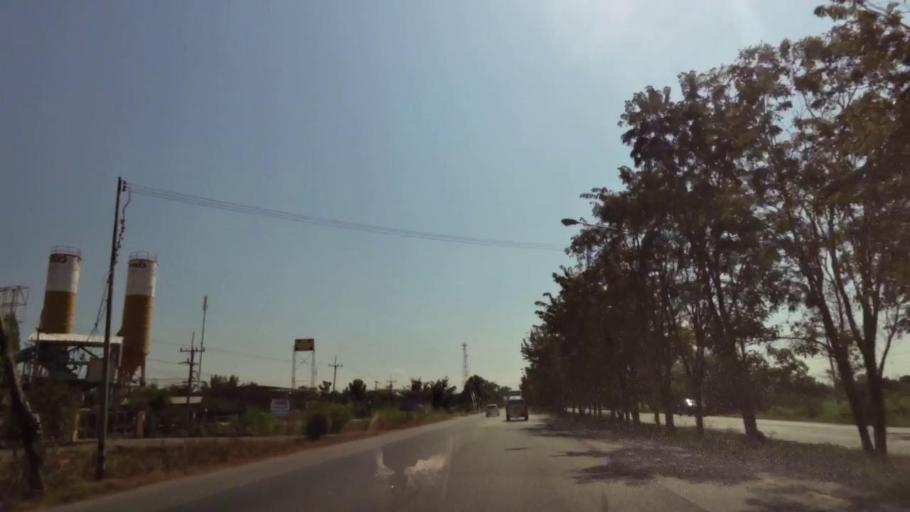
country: TH
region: Nakhon Sawan
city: Kao Liao
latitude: 15.8749
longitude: 100.1162
